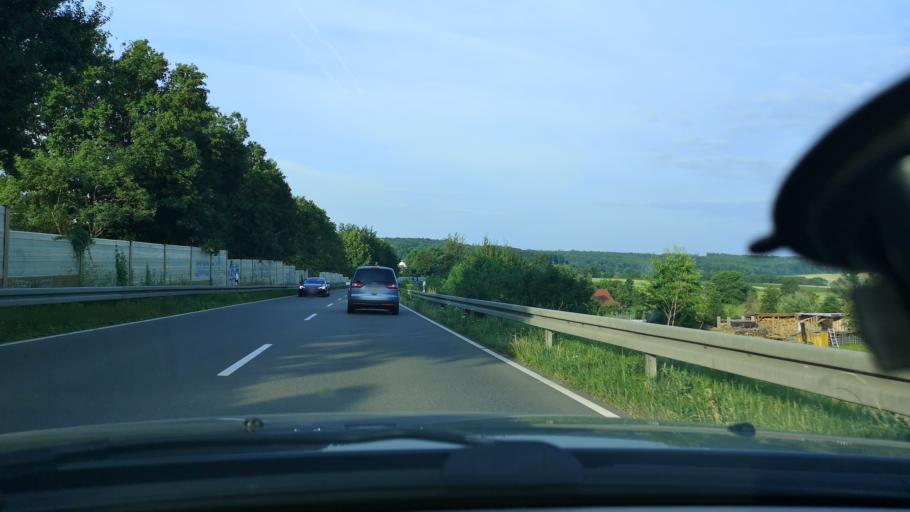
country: DE
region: Baden-Wuerttemberg
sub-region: Regierungsbezirk Stuttgart
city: Schlierbach
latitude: 48.6746
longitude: 9.5130
